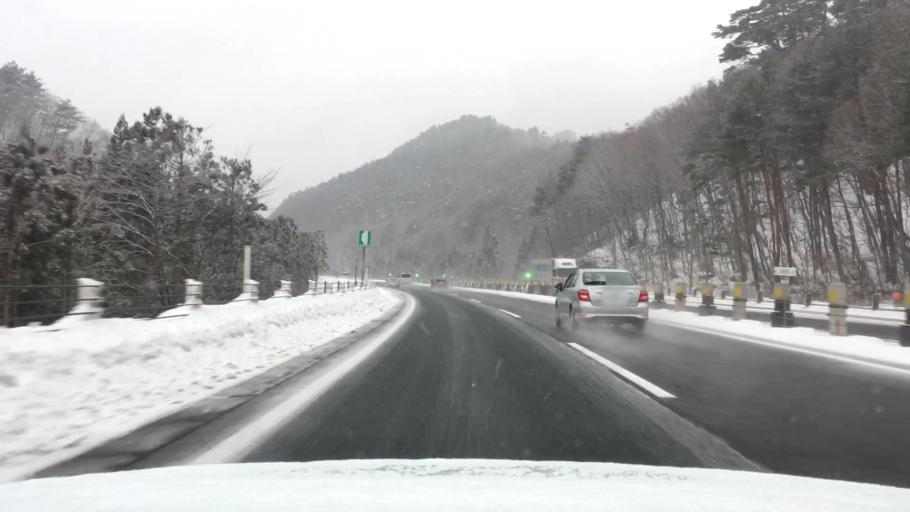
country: JP
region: Akita
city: Hanawa
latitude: 40.1159
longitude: 141.0306
